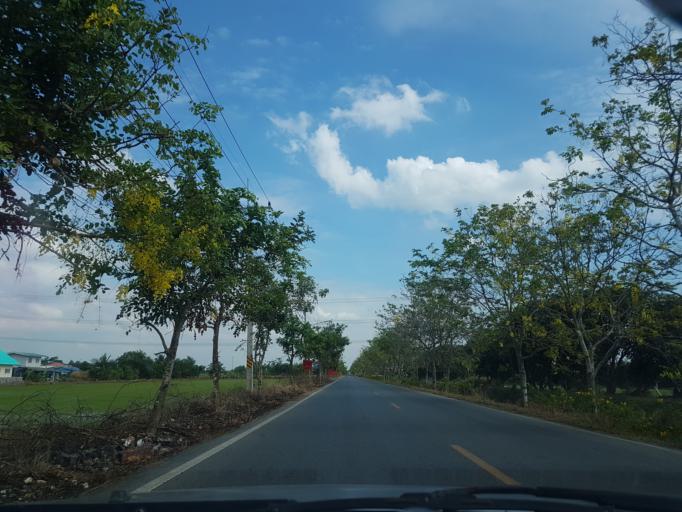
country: TH
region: Pathum Thani
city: Nong Suea
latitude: 14.1358
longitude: 100.8778
